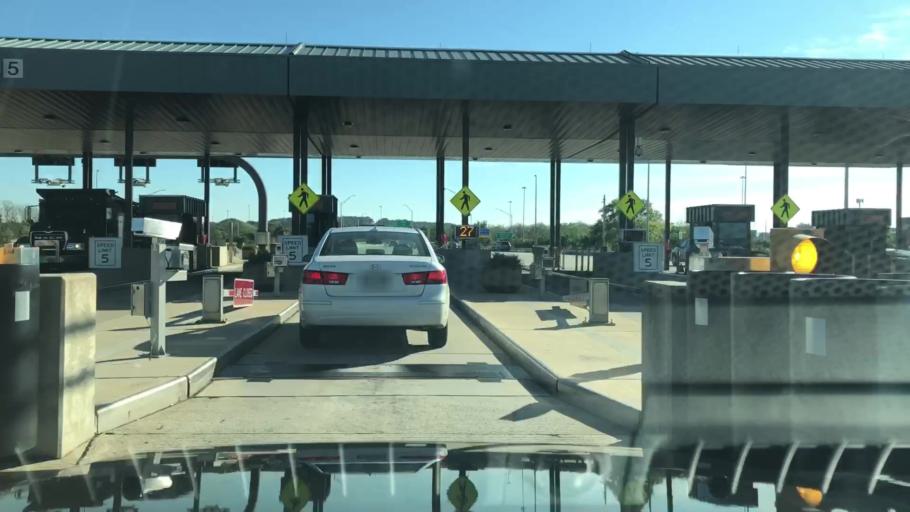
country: US
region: Pennsylvania
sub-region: Montgomery County
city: Plymouth Meeting
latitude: 40.1095
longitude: -75.2875
